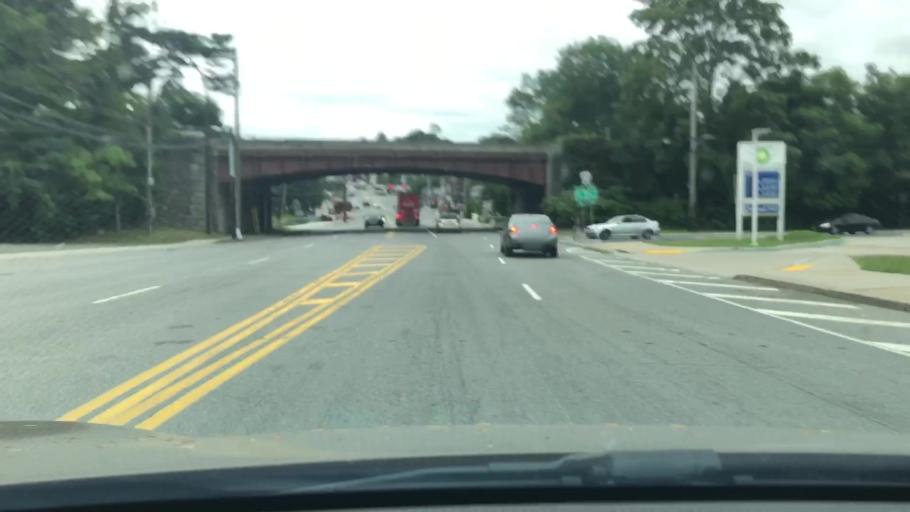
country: US
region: New York
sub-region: Westchester County
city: Elmsford
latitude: 41.0559
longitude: -73.8220
